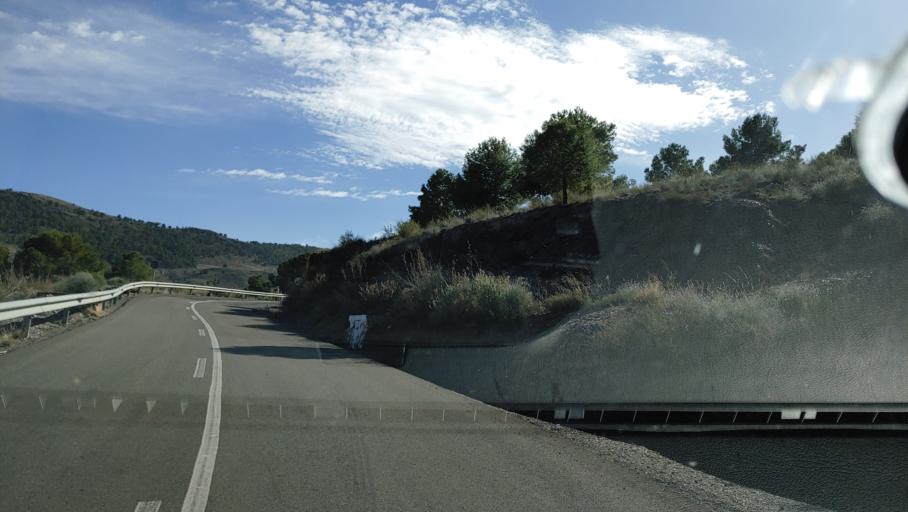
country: ES
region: Andalusia
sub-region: Provincia de Almeria
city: Alicun
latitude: 36.9430
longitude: -2.6032
